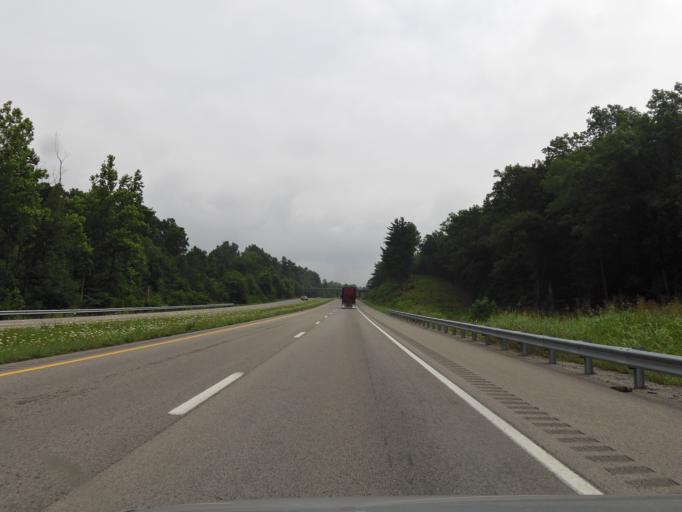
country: US
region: Kentucky
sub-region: Muhlenberg County
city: Central City
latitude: 37.3113
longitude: -87.0569
